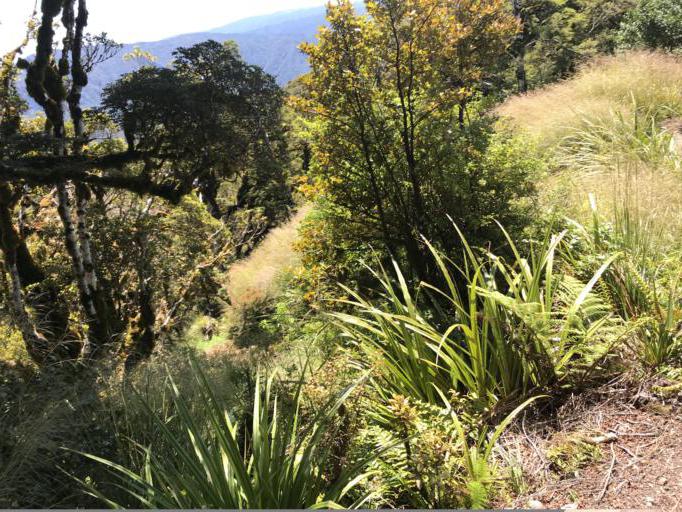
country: NZ
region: Wellington
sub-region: Kapiti Coast District
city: Otaki
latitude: -40.9079
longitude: 175.2562
